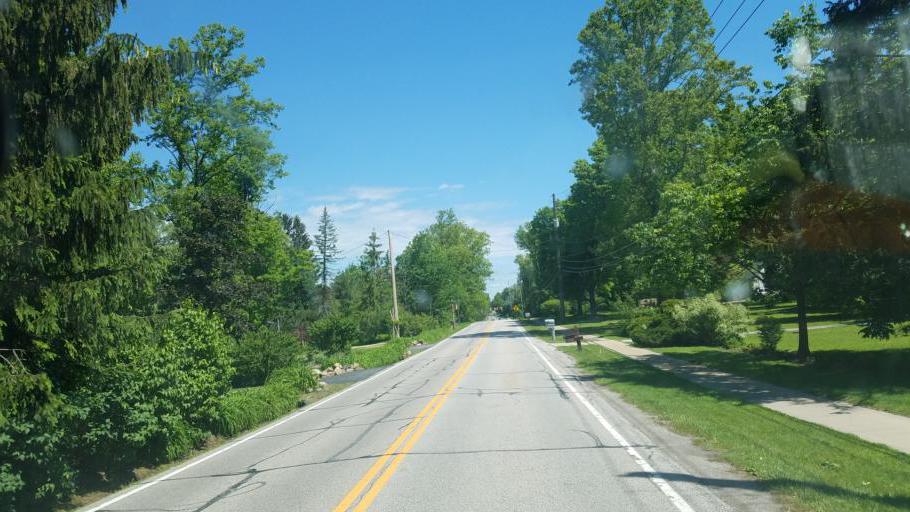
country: US
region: Ohio
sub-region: Geauga County
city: Bainbridge
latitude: 41.3963
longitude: -81.3079
